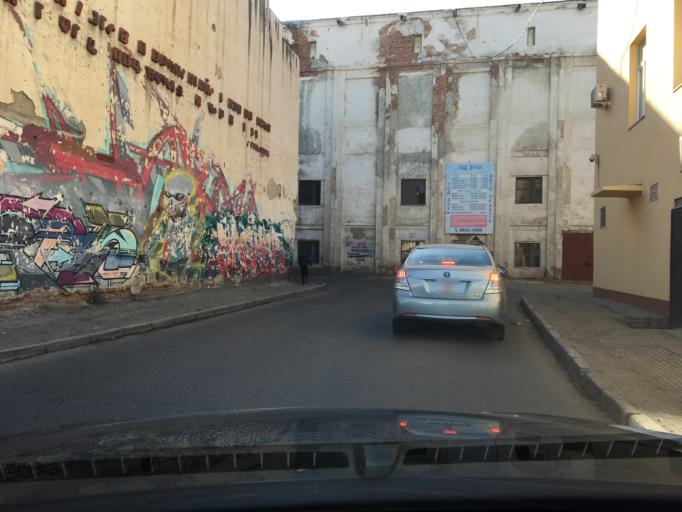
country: MN
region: Ulaanbaatar
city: Ulaanbaatar
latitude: 47.8944
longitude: 106.8961
